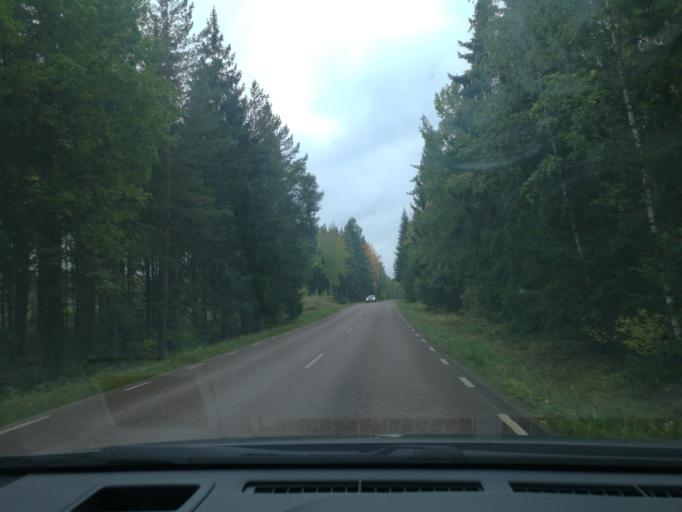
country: SE
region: Vaestmanland
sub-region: Vasteras
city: Tillberga
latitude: 59.7202
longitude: 16.6655
